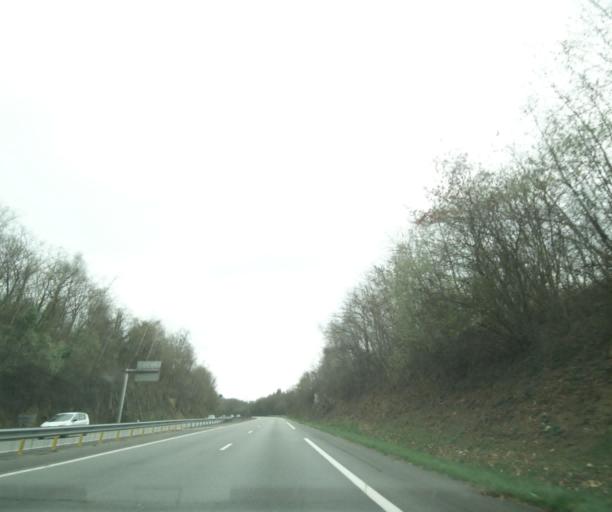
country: FR
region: Limousin
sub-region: Departement de la Haute-Vienne
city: Condat-sur-Vienne
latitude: 45.8021
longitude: 1.2964
